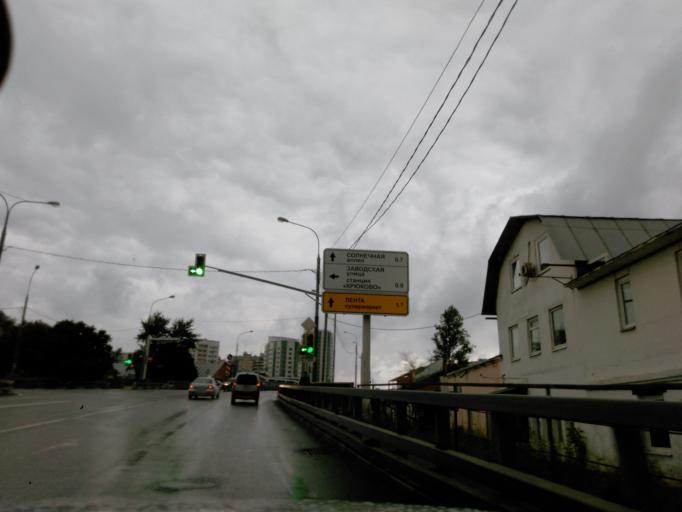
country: RU
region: Moscow
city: Zelenograd
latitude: 55.9741
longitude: 37.1834
